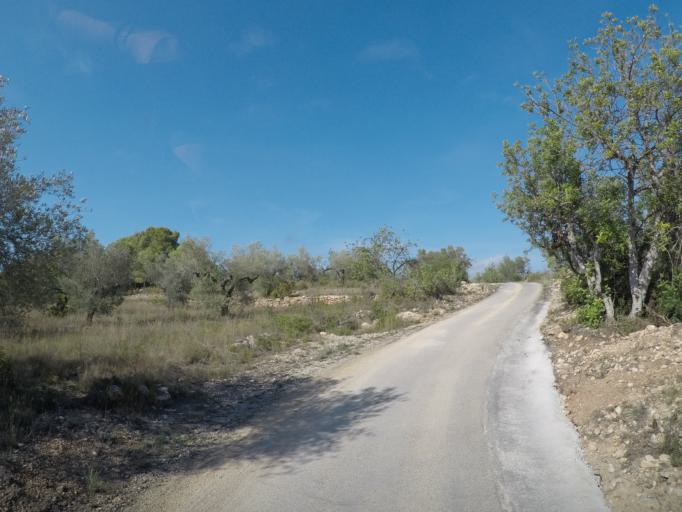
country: ES
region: Catalonia
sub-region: Provincia de Tarragona
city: El Perello
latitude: 40.9049
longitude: 0.7264
